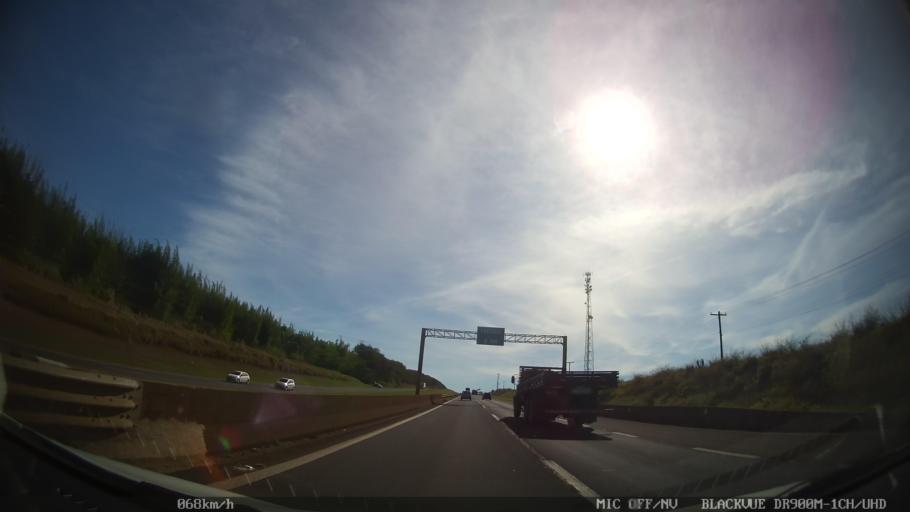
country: BR
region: Sao Paulo
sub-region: Leme
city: Leme
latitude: -22.2712
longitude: -47.3917
